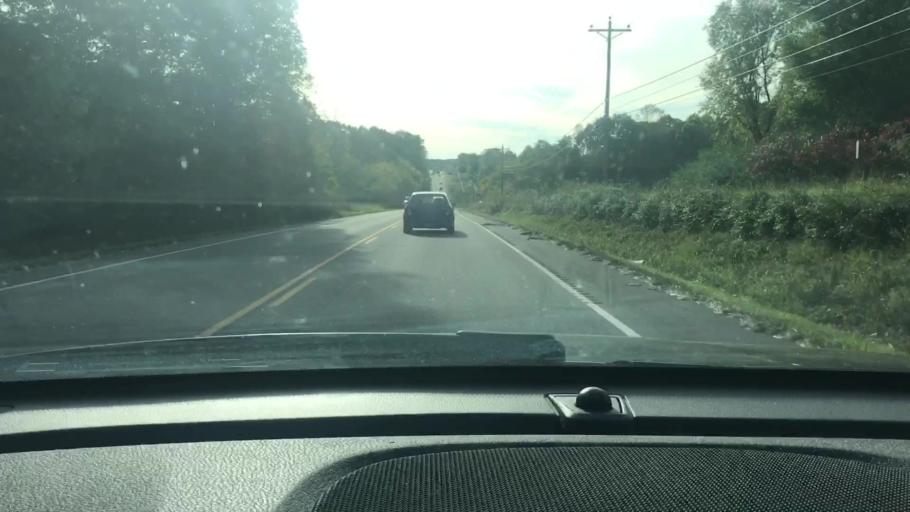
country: US
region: Tennessee
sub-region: Williamson County
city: Fairview
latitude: 35.9886
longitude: -87.1005
